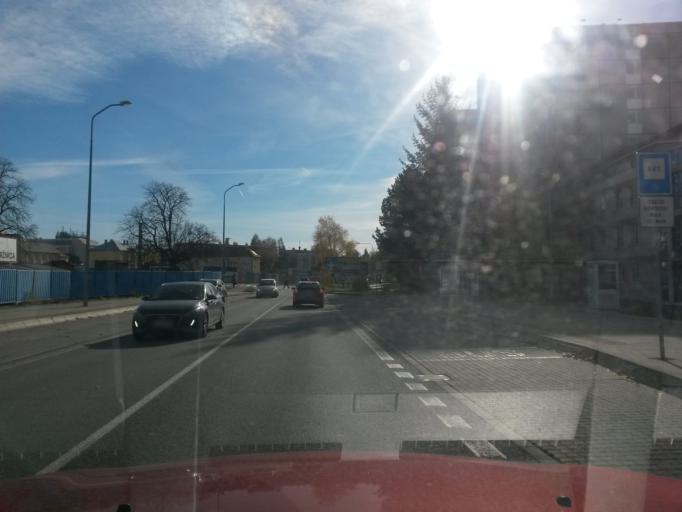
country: SK
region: Presovsky
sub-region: Okres Presov
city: Presov
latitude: 48.9935
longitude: 21.2399
